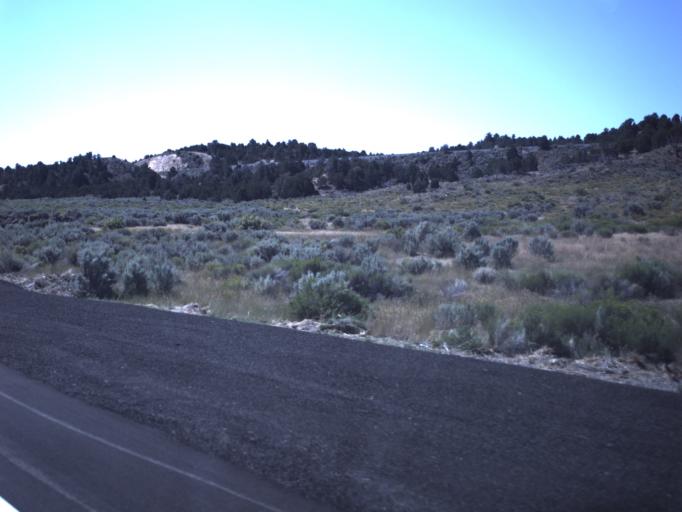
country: US
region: Utah
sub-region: Utah County
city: Eagle Mountain
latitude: 39.9951
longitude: -112.2706
